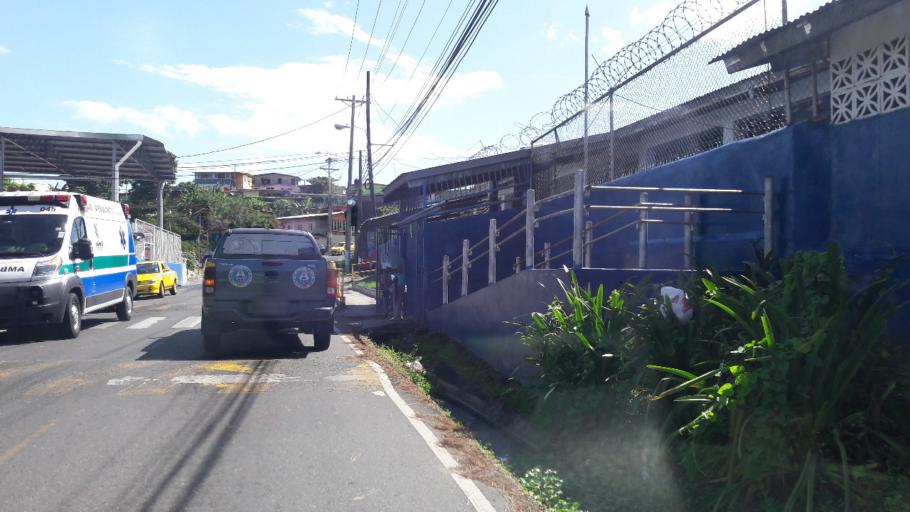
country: PA
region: Panama
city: San Miguelito
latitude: 9.0451
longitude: -79.5044
